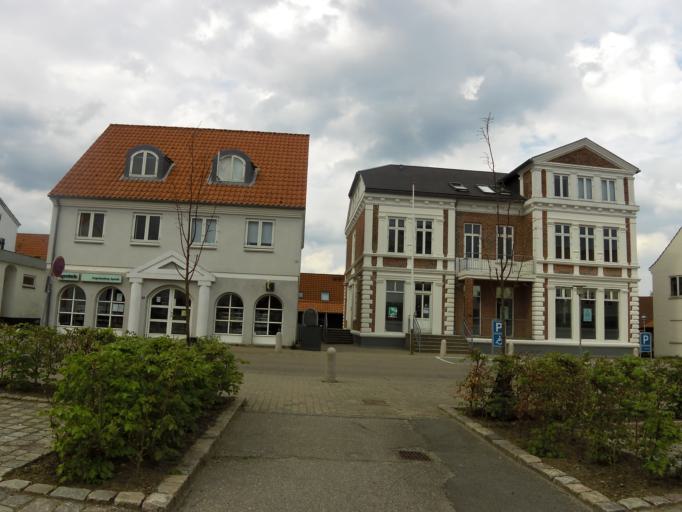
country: DK
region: South Denmark
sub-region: Sonderborg Kommune
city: Augustenborg
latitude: 54.9459
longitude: 9.8715
